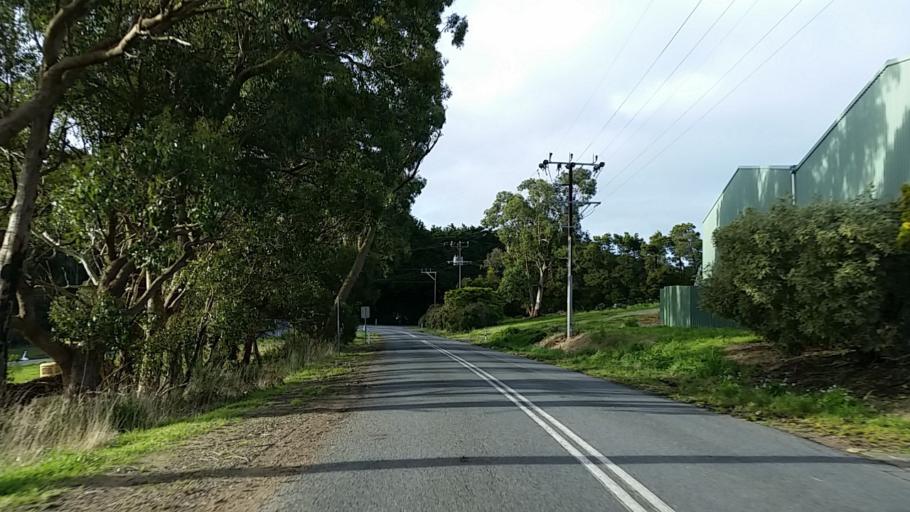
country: AU
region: South Australia
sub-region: Adelaide Hills
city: Bridgewater
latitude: -34.9566
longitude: 138.7544
